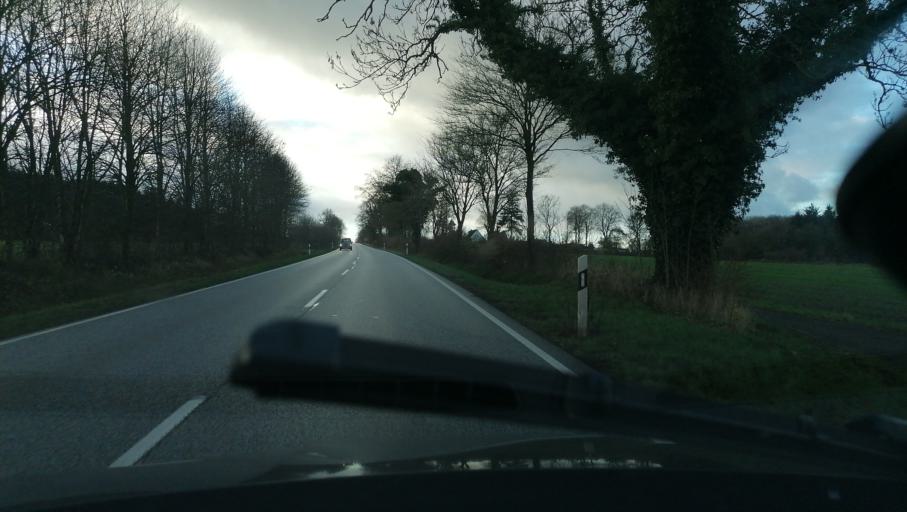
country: DE
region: Schleswig-Holstein
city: Tensbuttel-Rost
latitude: 54.1135
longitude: 9.2334
